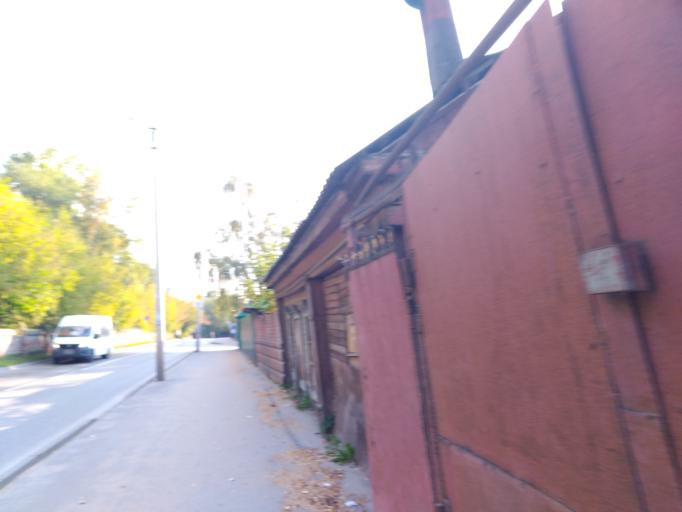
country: RU
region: Kaluga
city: Kaluga
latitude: 54.5238
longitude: 36.2530
